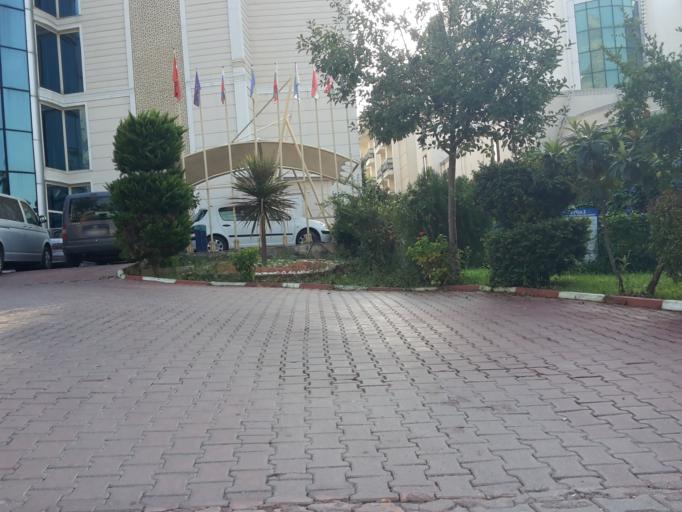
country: TR
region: Antalya
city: Kemer
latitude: 36.6145
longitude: 30.5563
